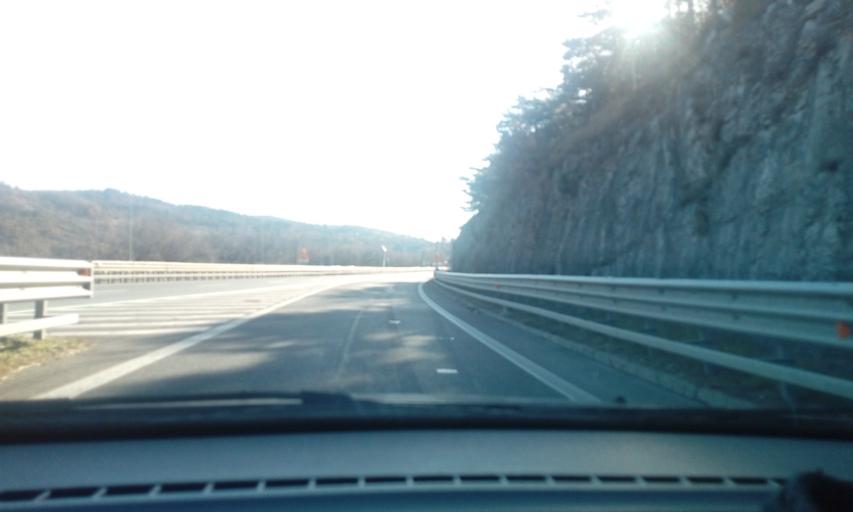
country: IT
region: Friuli Venezia Giulia
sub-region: Provincia di Trieste
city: Duino
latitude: 45.8017
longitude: 13.5811
